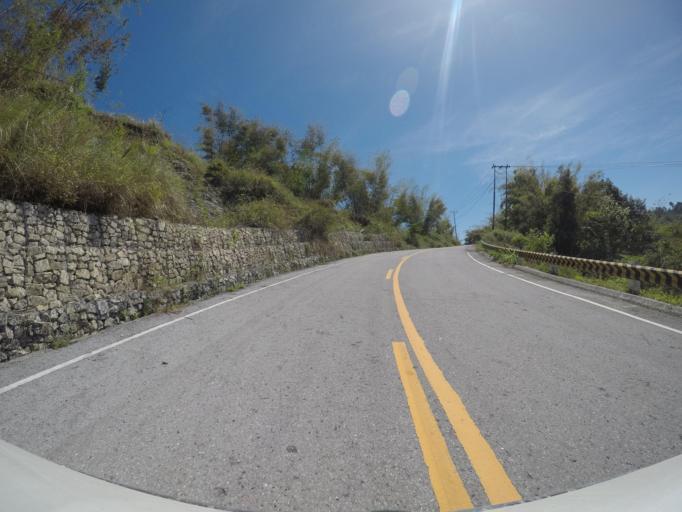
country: TL
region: Manufahi
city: Same
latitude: -8.8785
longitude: 125.9893
